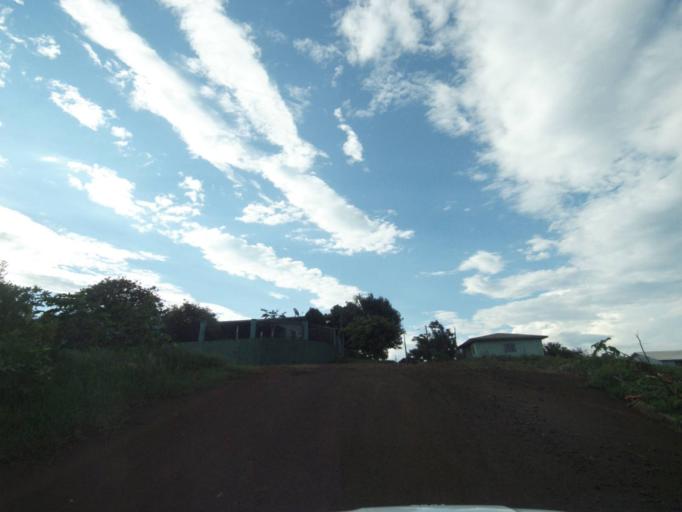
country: BR
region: Parana
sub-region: Laranjeiras Do Sul
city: Laranjeiras do Sul
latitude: -25.4889
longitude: -52.5226
